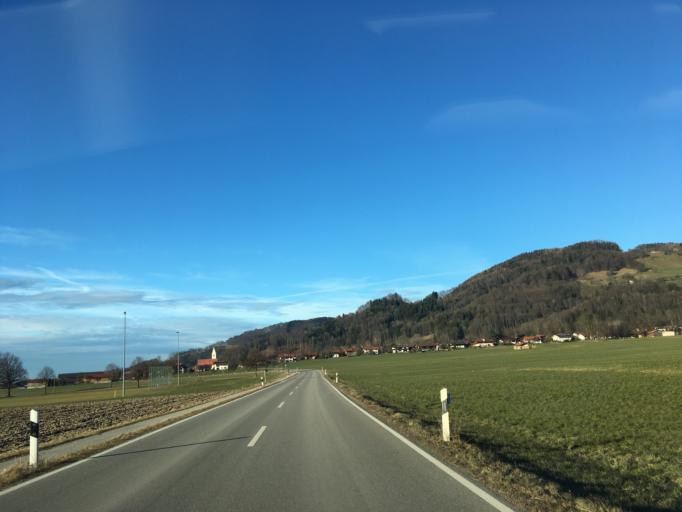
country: DE
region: Bavaria
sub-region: Upper Bavaria
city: Nussdorf am Inn
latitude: 47.7333
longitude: 12.1606
